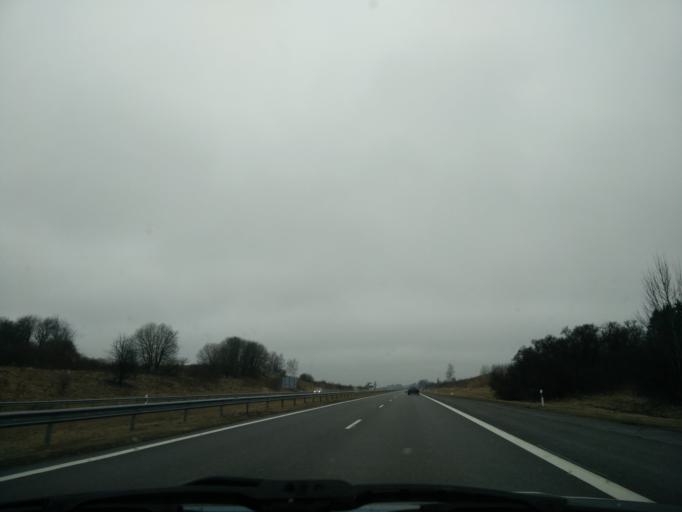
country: LT
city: Skaudvile
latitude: 55.4494
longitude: 22.7154
